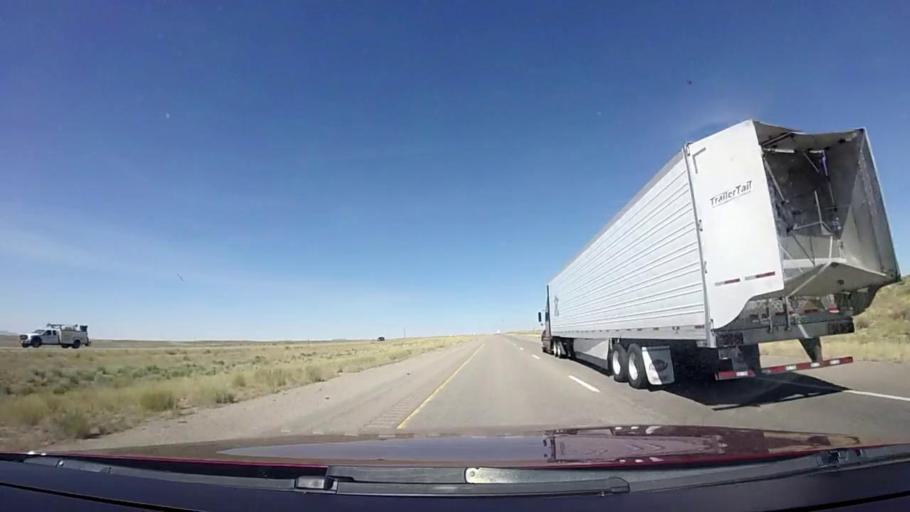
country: US
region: Wyoming
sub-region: Sweetwater County
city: Rock Springs
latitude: 41.6378
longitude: -108.4464
